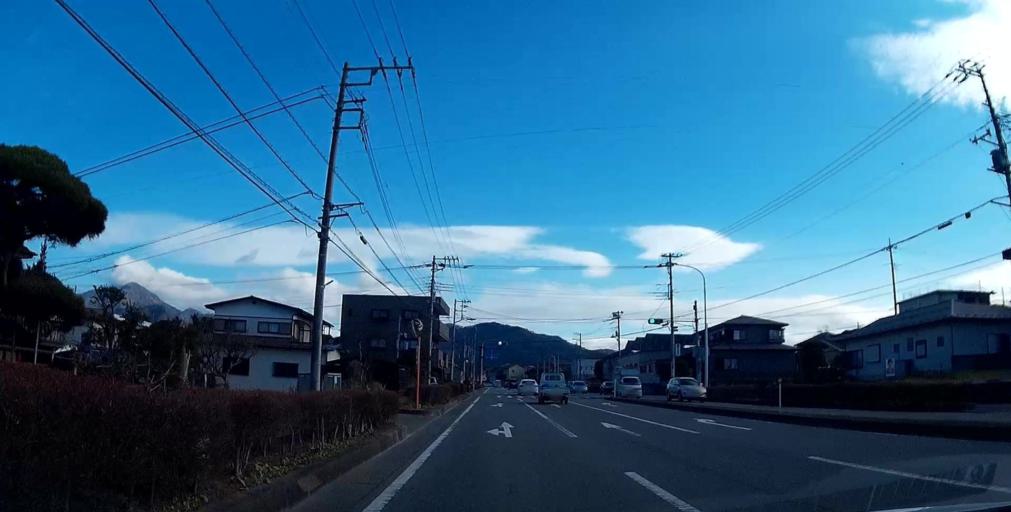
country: JP
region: Yamanashi
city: Fujikawaguchiko
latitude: 35.4875
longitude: 138.7985
